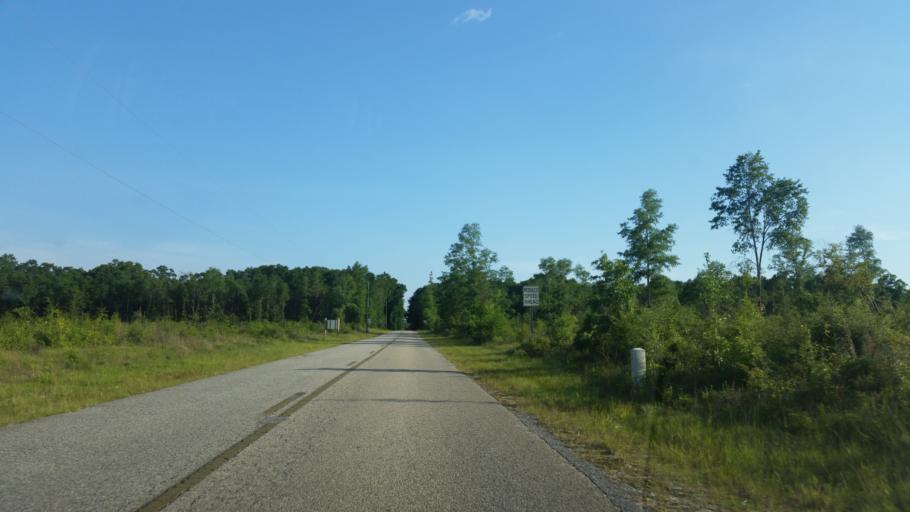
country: US
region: Florida
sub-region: Santa Rosa County
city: East Milton
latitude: 30.6645
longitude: -86.8788
